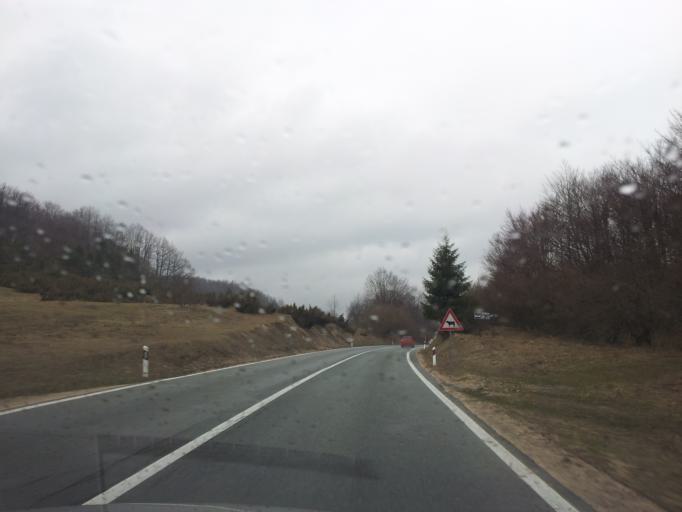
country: HR
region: Licko-Senjska
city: Jezerce
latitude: 44.8434
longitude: 15.6588
